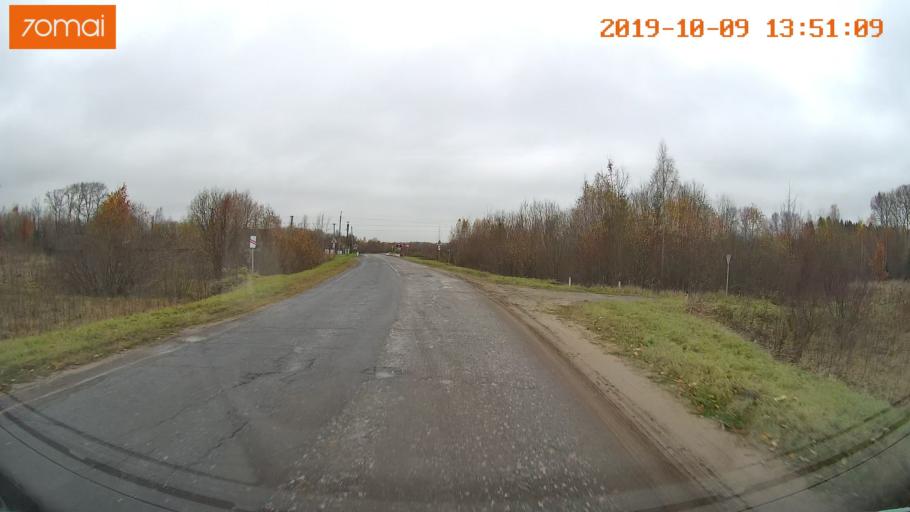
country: RU
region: Kostroma
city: Buy
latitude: 58.4064
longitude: 41.2417
